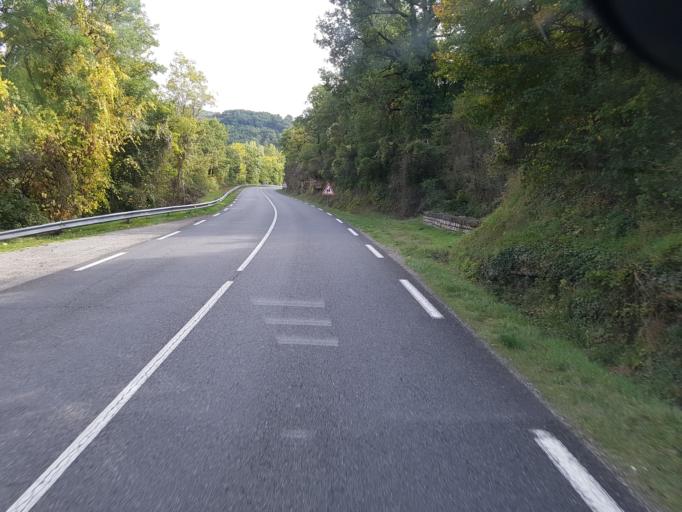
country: FR
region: Midi-Pyrenees
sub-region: Departement de l'Aveyron
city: Saint-Georges-de-Luzencon
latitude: 44.0316
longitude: 2.9626
